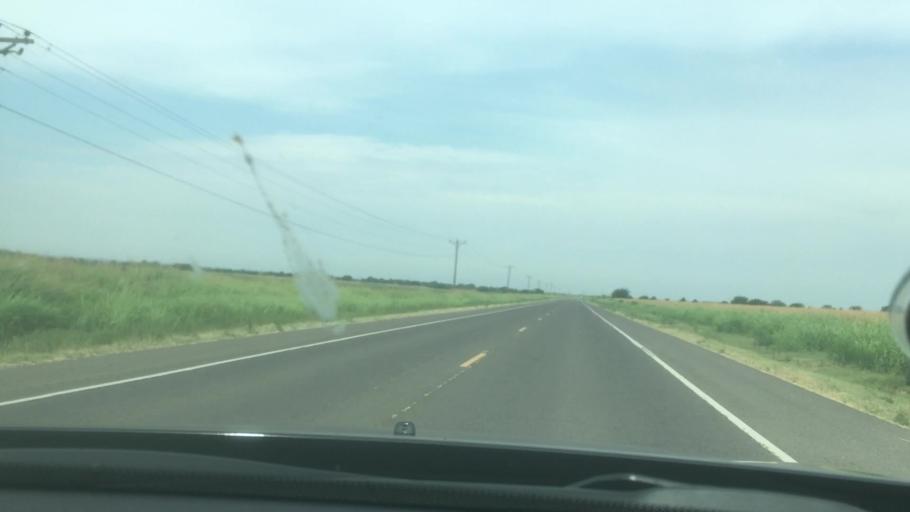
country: US
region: Oklahoma
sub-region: Garvin County
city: Maysville
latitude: 34.8192
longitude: -97.4772
